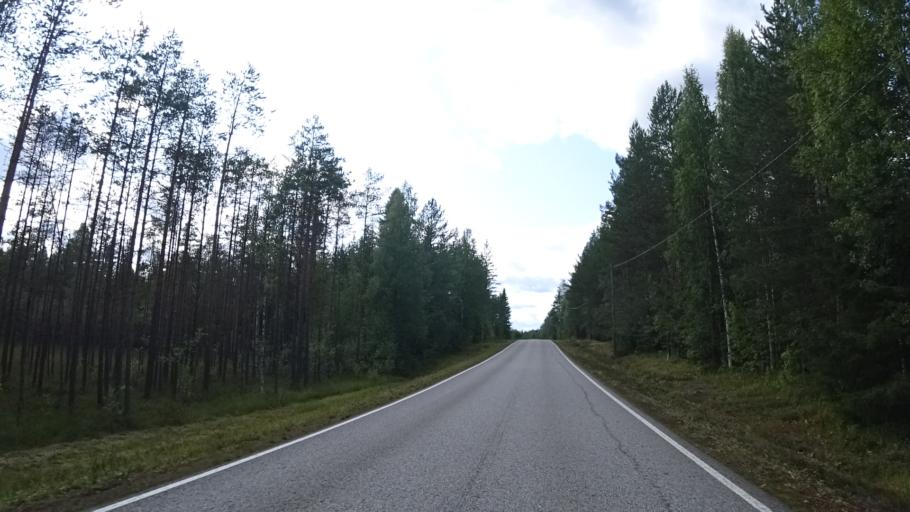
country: RU
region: Republic of Karelia
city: Vyartsilya
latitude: 62.2569
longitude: 30.7599
